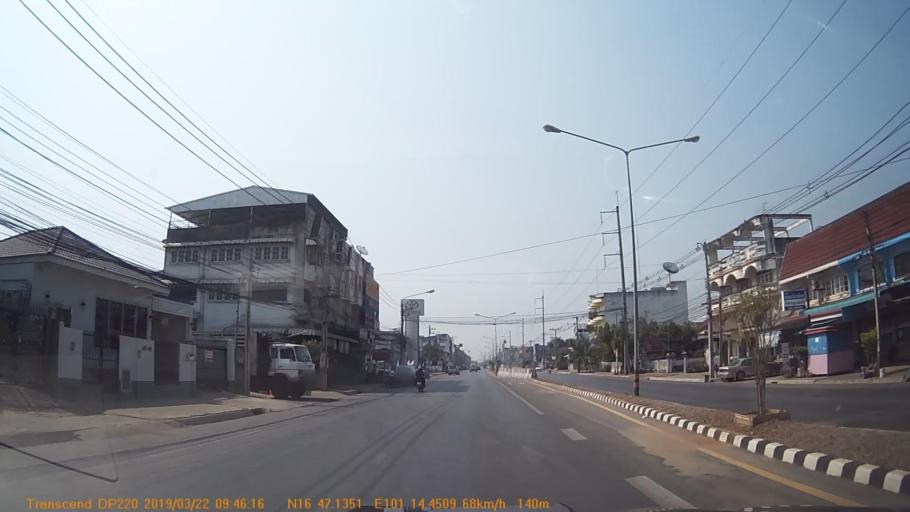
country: TH
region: Phetchabun
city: Lom Sak
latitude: 16.7851
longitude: 101.2409
